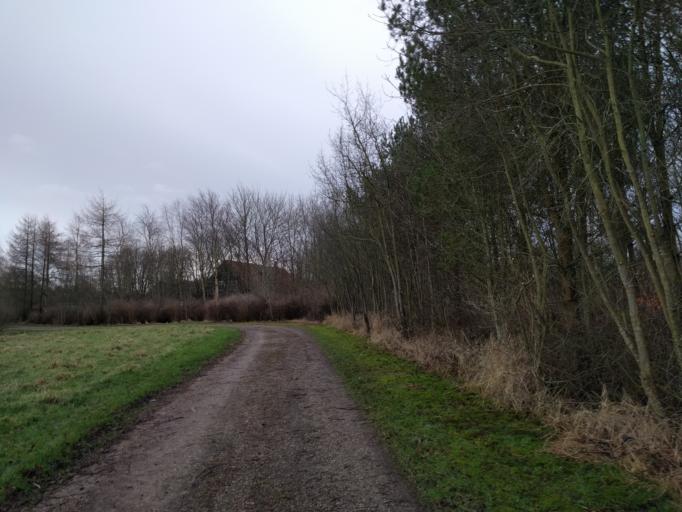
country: DK
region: Central Jutland
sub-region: Viborg Kommune
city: Viborg
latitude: 56.4432
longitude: 9.4247
